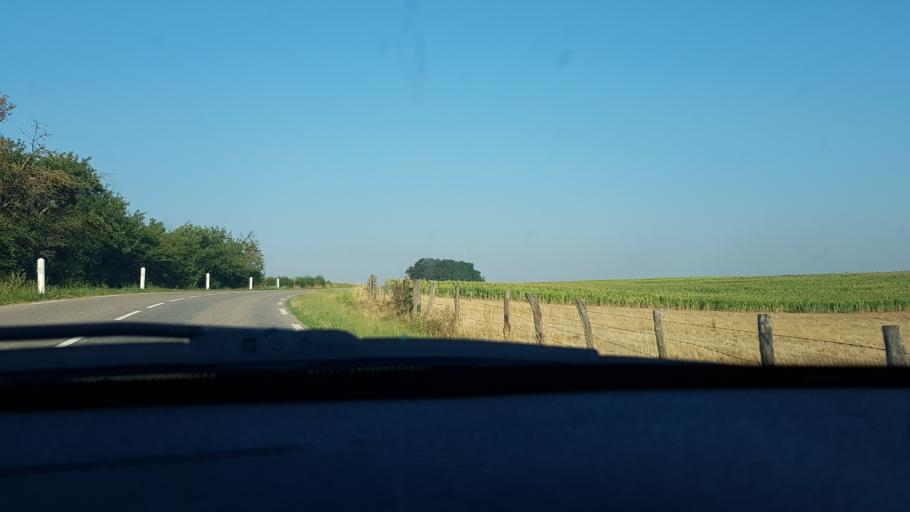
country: FR
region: Lorraine
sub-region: Departement des Vosges
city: Charmes
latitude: 48.3568
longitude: 6.2060
